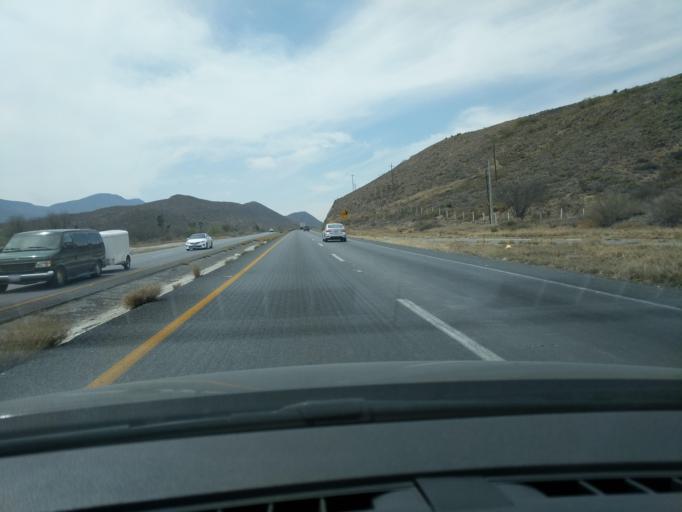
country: MX
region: Coahuila
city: Saltillo
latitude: 25.4531
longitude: -101.0824
